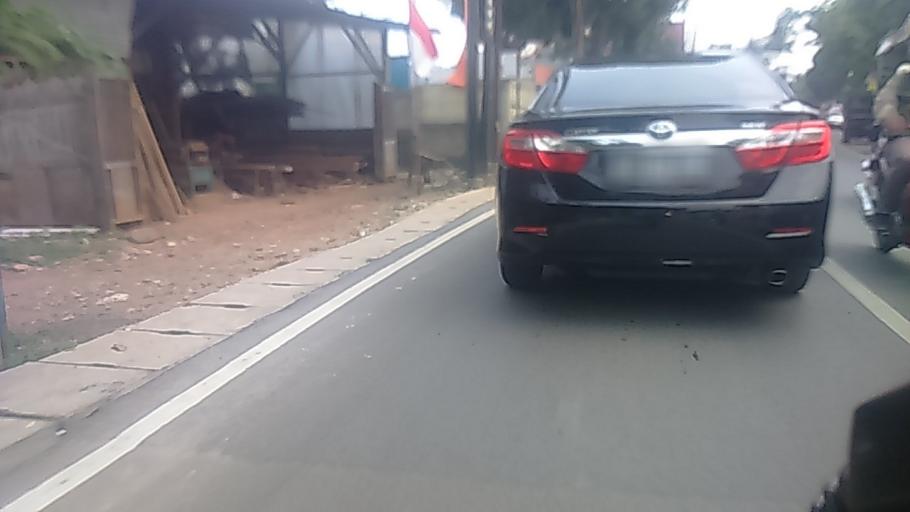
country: ID
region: West Java
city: Depok
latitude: -6.3353
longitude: 106.8067
